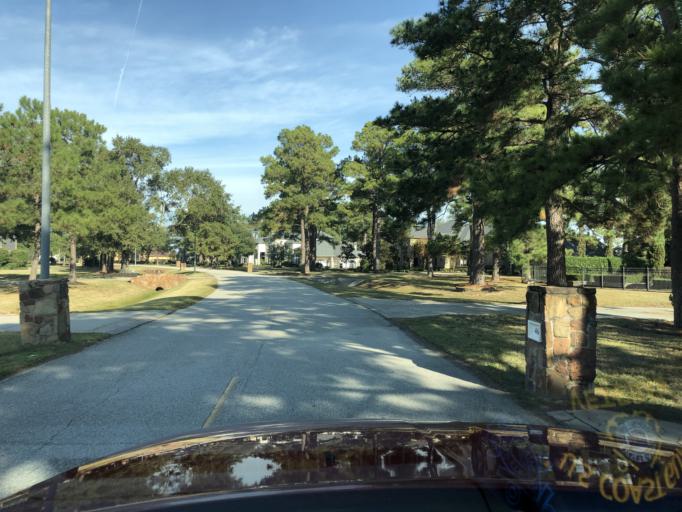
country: US
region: Texas
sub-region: Harris County
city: Tomball
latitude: 30.0408
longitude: -95.5575
